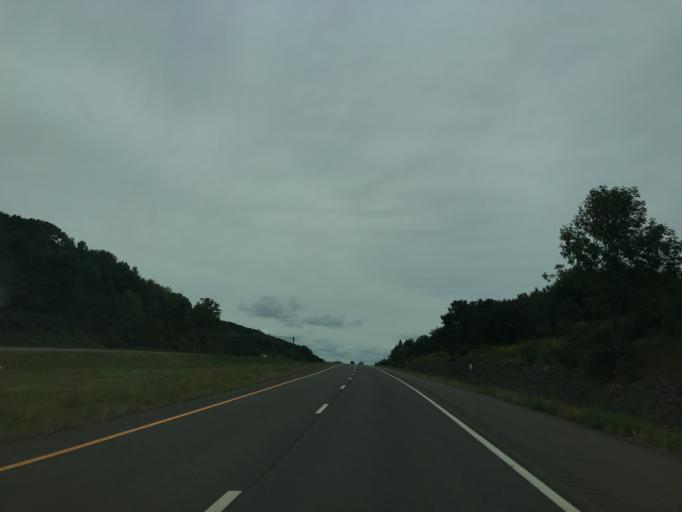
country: US
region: New York
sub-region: Chenango County
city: Greene
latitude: 42.1879
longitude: -75.6868
